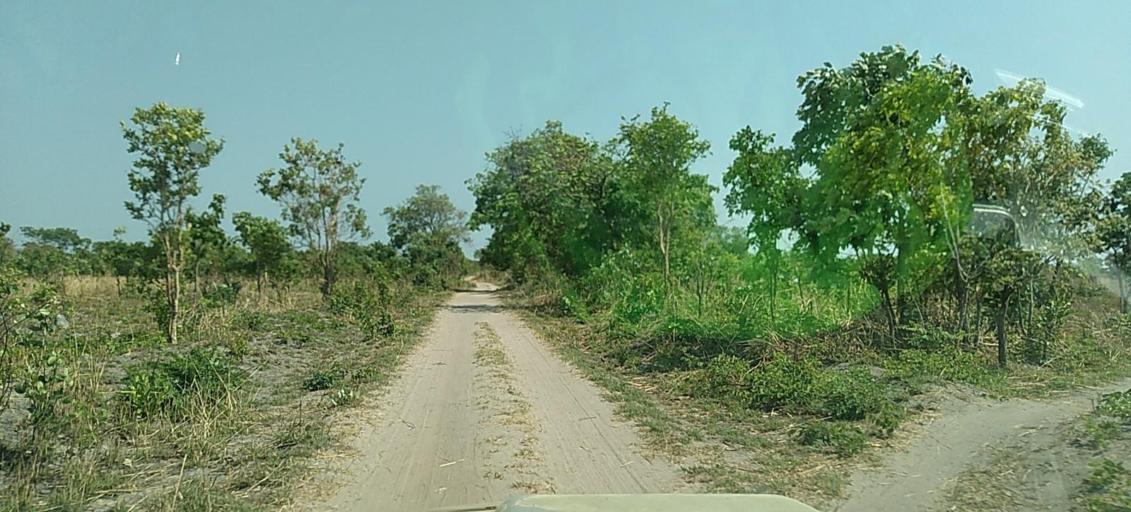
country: ZM
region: North-Western
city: Kalengwa
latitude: -13.2358
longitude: 24.7533
